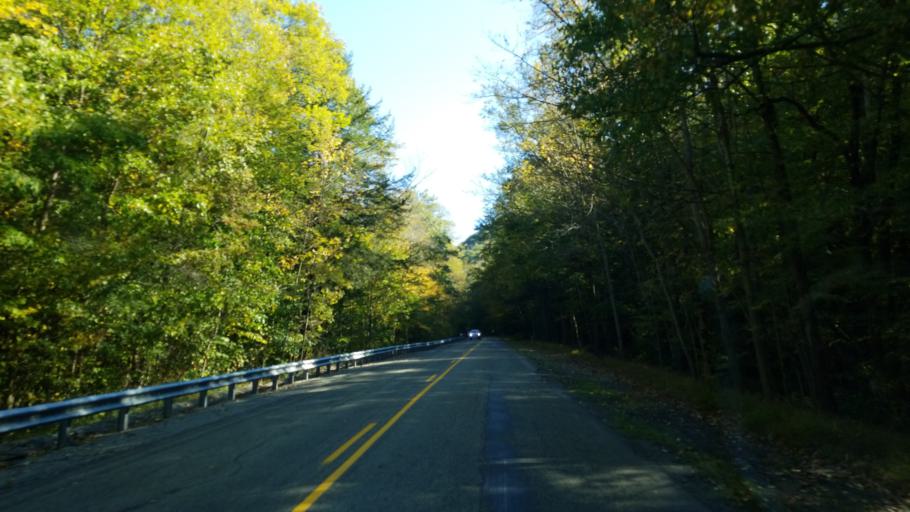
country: US
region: Pennsylvania
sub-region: Clearfield County
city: Shiloh
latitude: 41.2569
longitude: -78.3869
